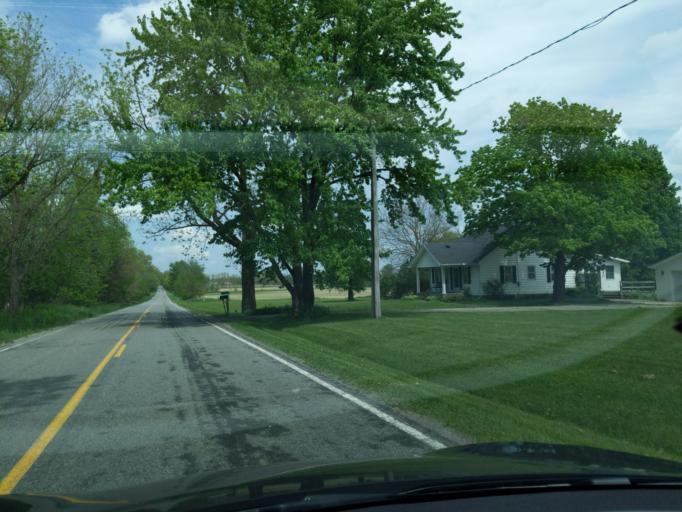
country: US
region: Michigan
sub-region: Ingham County
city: Stockbridge
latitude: 42.4924
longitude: -84.1601
